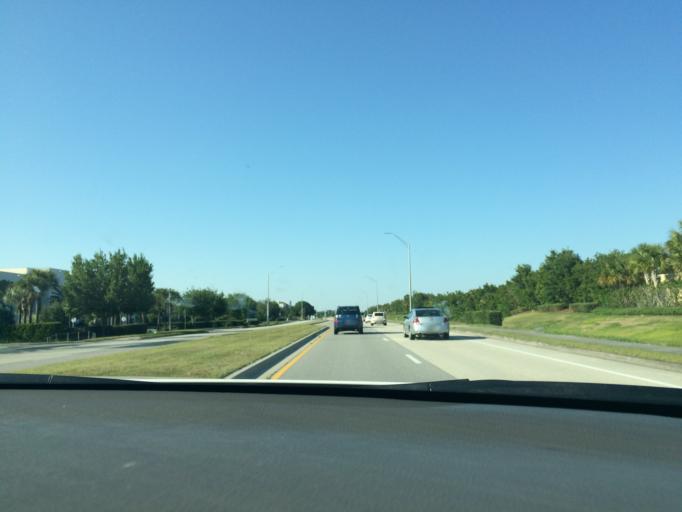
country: US
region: Florida
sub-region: Sarasota County
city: The Meadows
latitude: 27.4502
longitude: -82.4324
